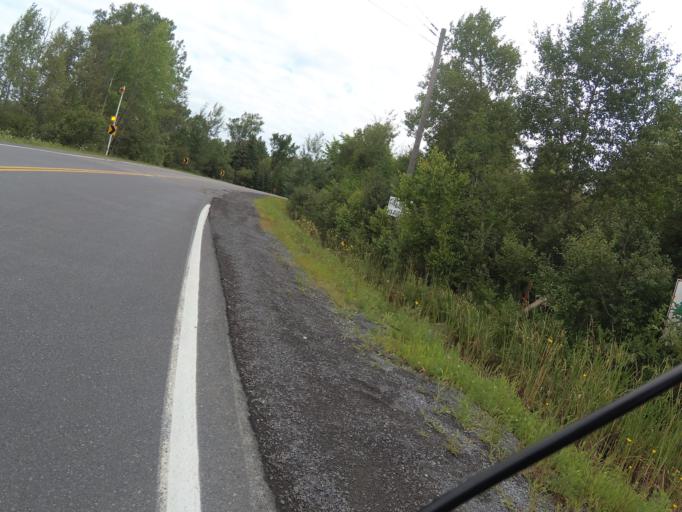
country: CA
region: Ontario
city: Bourget
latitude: 45.3533
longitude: -75.2781
